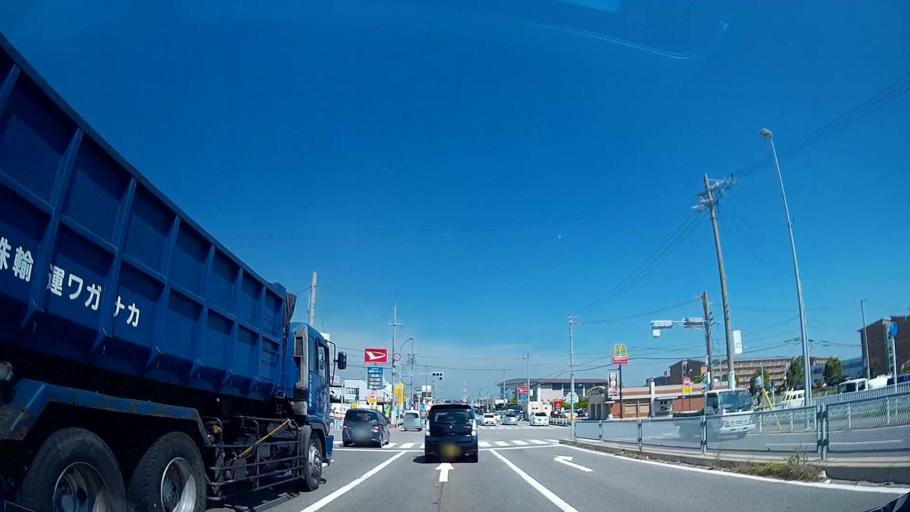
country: JP
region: Aichi
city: Hekinan
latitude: 34.8638
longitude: 136.9860
